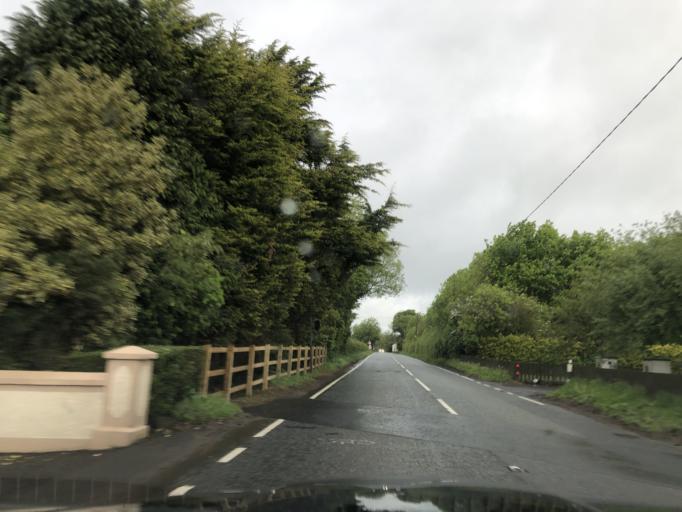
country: GB
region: Northern Ireland
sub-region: Antrim Borough
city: Antrim
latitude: 54.6754
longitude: -6.2215
